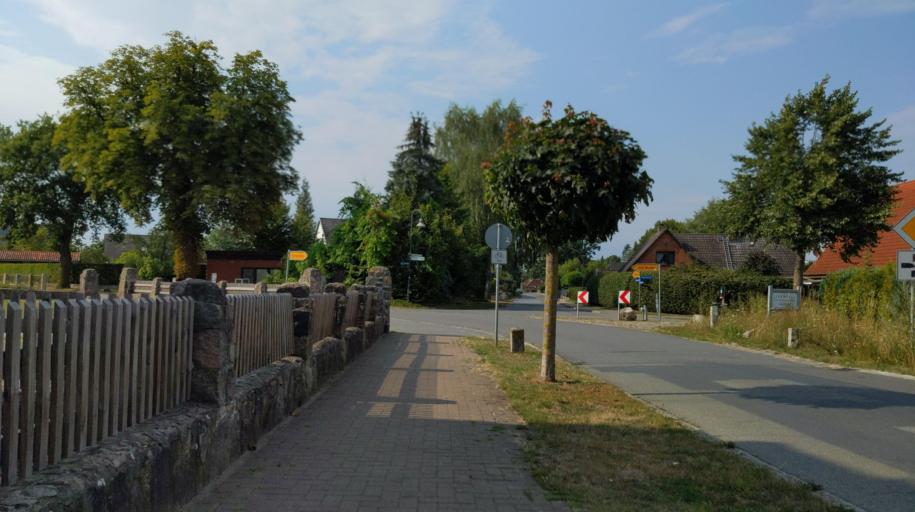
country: DE
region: Schleswig-Holstein
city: Rondeshagen
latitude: 53.7532
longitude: 10.6299
